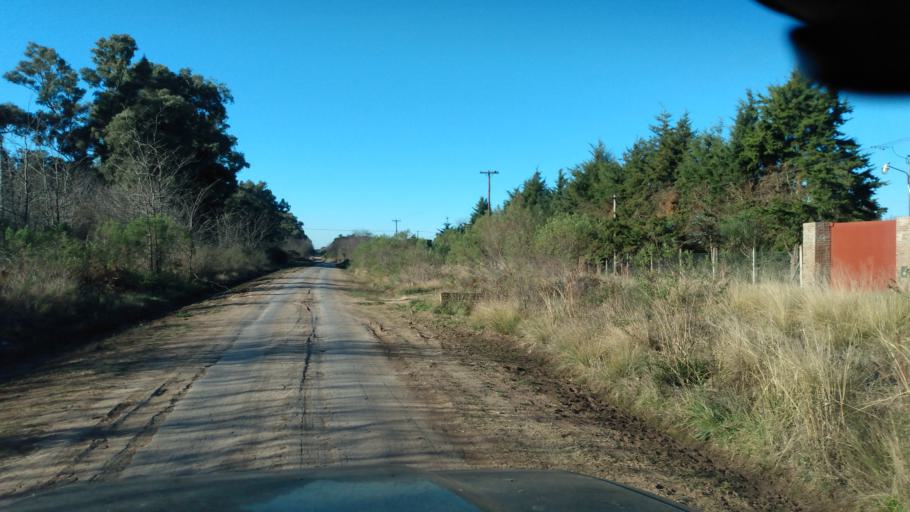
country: AR
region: Buenos Aires
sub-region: Partido de Lujan
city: Lujan
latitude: -34.5595
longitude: -59.1589
